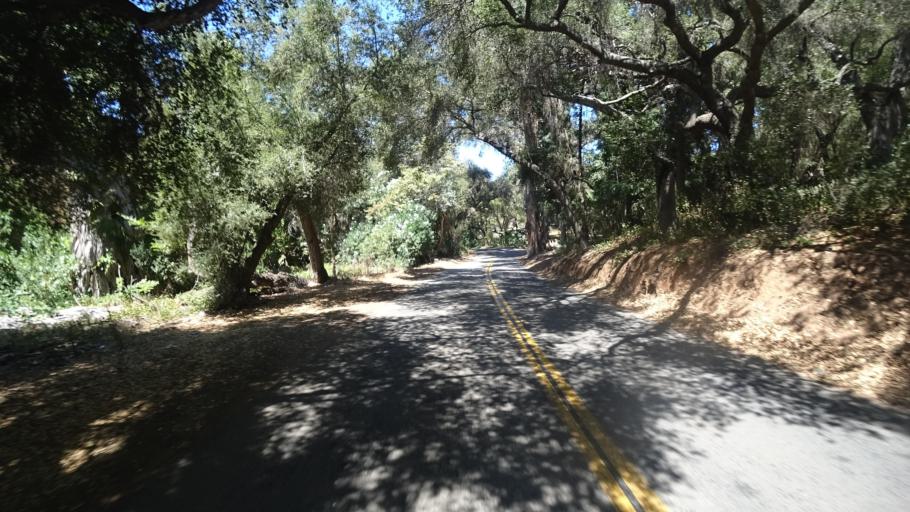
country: US
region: California
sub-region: San Diego County
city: Hidden Meadows
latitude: 33.3194
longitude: -117.1019
